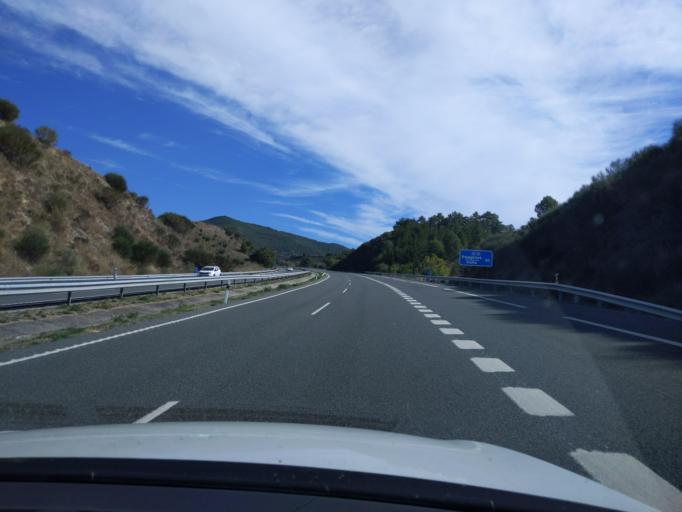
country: ES
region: Navarre
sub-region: Provincia de Navarra
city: Cirauqui
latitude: 42.6745
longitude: -1.9087
